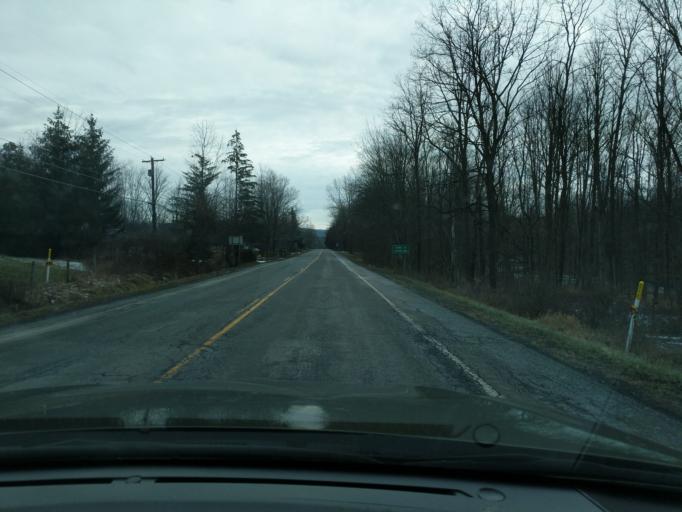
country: US
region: New York
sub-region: Tompkins County
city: East Ithaca
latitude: 42.3974
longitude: -76.4215
